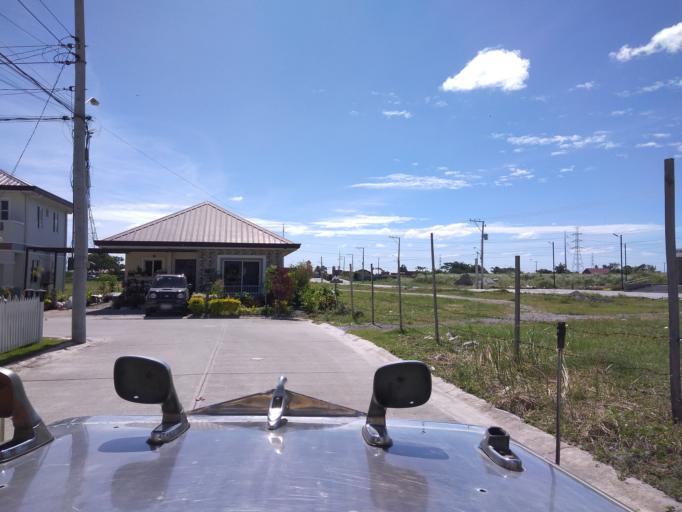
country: PH
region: Central Luzon
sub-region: Province of Pampanga
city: San Juan
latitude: 15.0200
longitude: 120.6632
